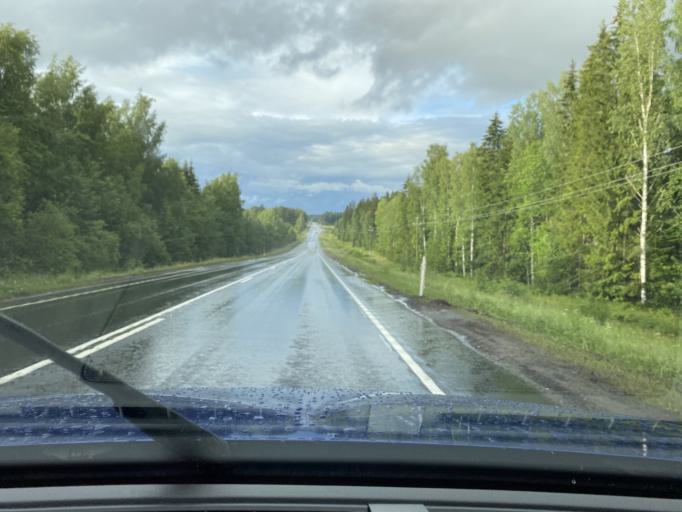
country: FI
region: Uusimaa
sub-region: Helsinki
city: Nurmijaervi
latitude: 60.4661
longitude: 24.8367
